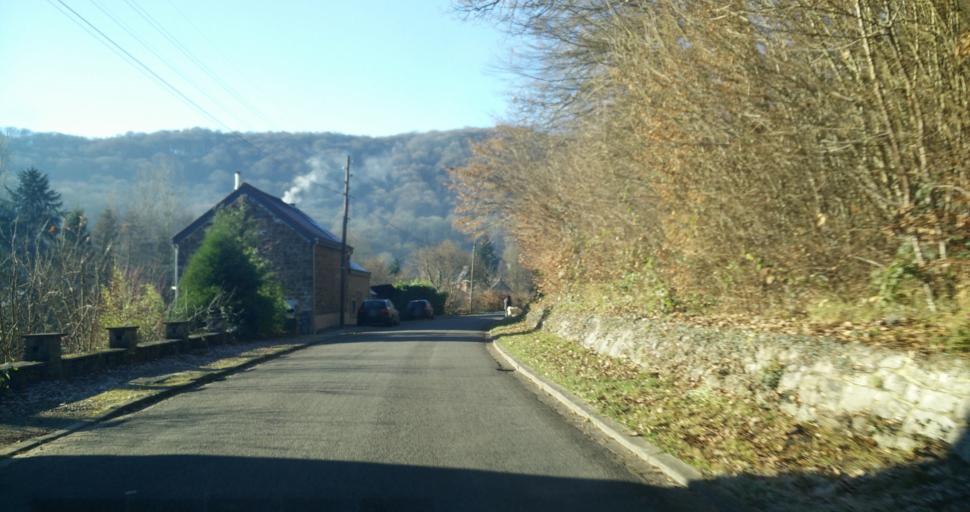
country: BE
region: Wallonia
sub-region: Province de Namur
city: Profondeville
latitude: 50.3775
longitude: 4.8609
